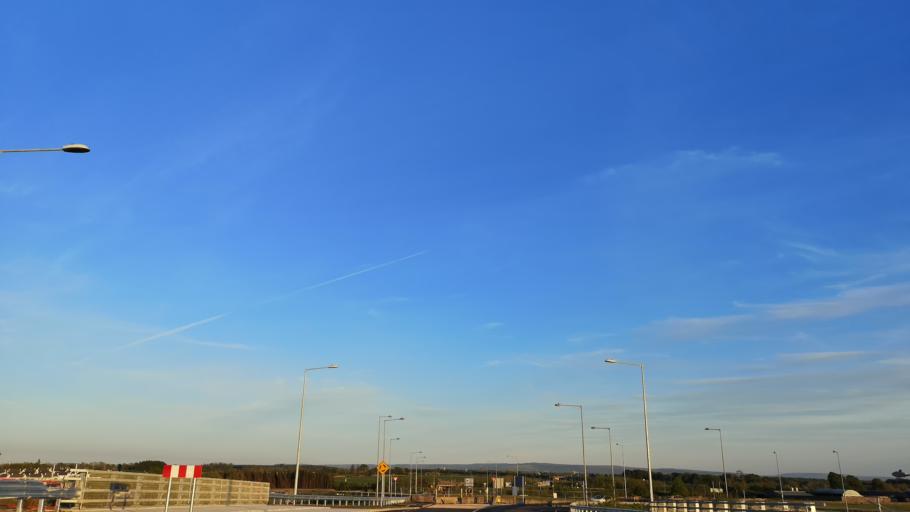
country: IE
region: Connaught
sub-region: County Galway
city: Athenry
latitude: 53.2949
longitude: -8.7597
